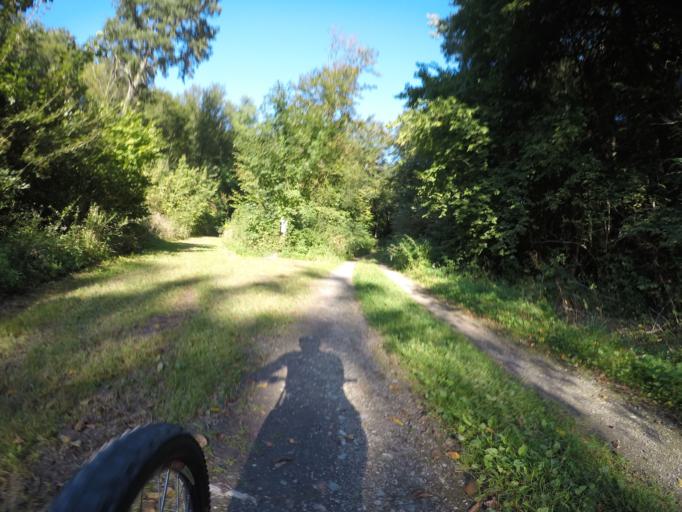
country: AT
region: Lower Austria
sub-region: Politischer Bezirk Bruck an der Leitha
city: Mannersdorf am Leithagebirge
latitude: 47.9581
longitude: 16.6088
